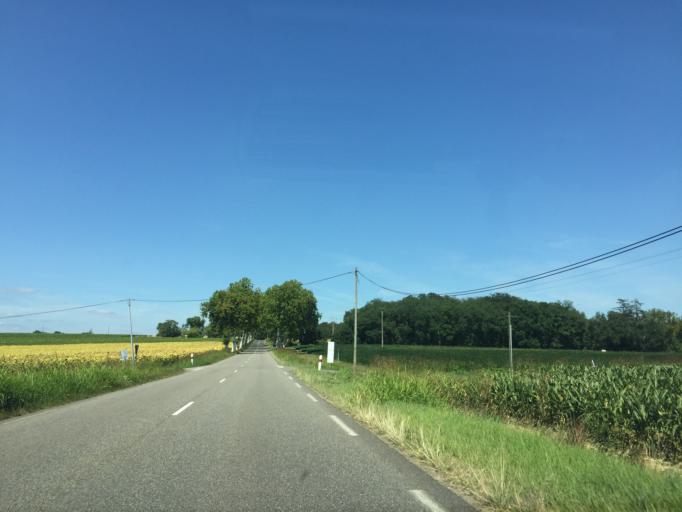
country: FR
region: Aquitaine
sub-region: Departement du Lot-et-Garonne
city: Mezin
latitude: 44.0703
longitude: 0.2744
